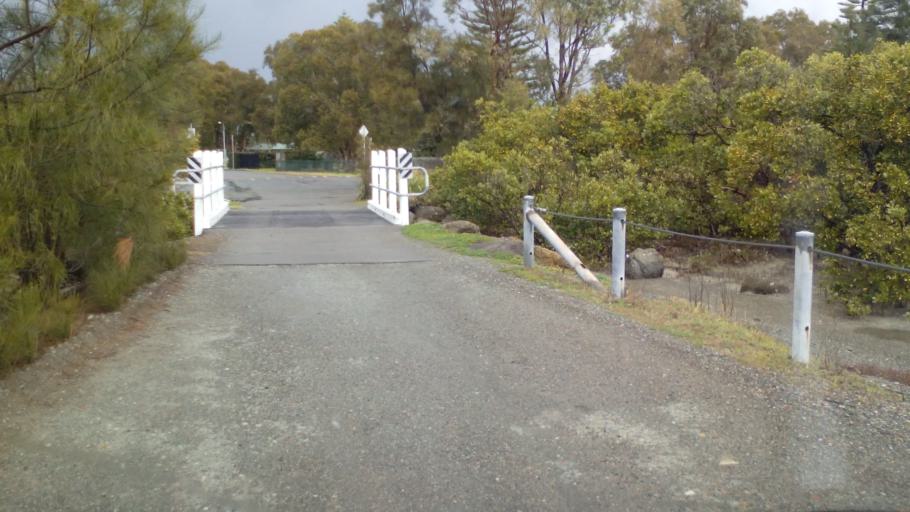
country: AU
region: New South Wales
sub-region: Lake Macquarie Shire
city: Belmont South
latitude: -33.0740
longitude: 151.6375
